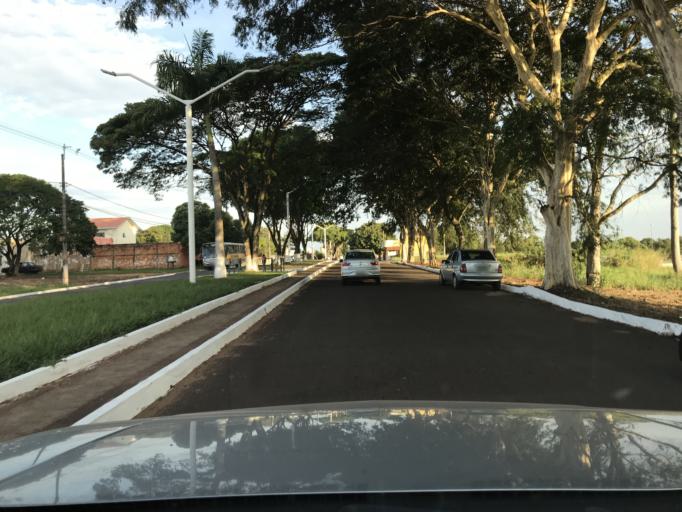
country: BR
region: Mato Grosso do Sul
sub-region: Iguatemi
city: Iguatemi
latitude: -23.6715
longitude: -54.5611
